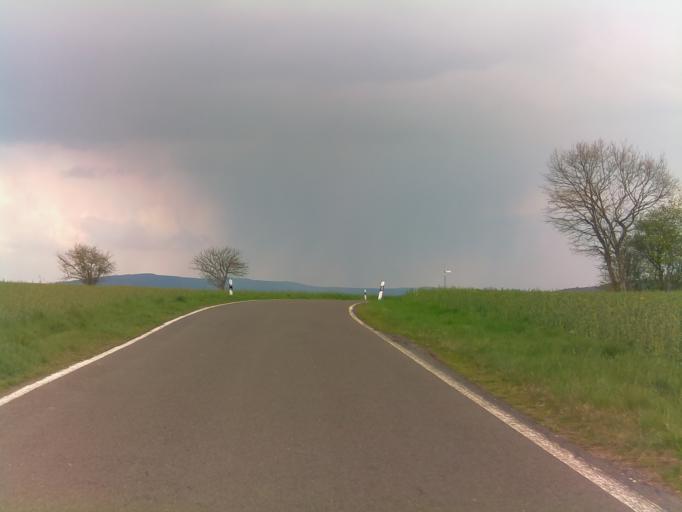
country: DE
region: Rheinland-Pfalz
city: Daubach
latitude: 49.8543
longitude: 7.6276
